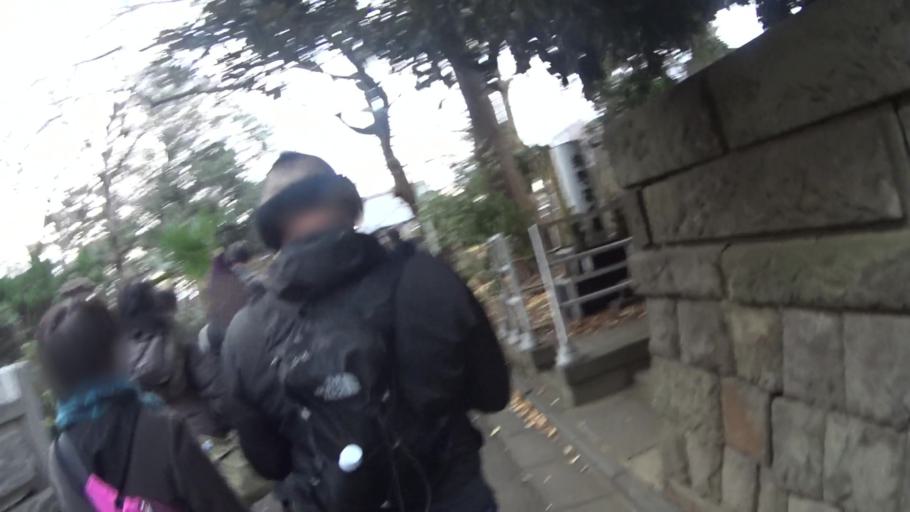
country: JP
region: Kanagawa
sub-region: Kawasaki-shi
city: Kawasaki
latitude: 35.5776
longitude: 139.7059
